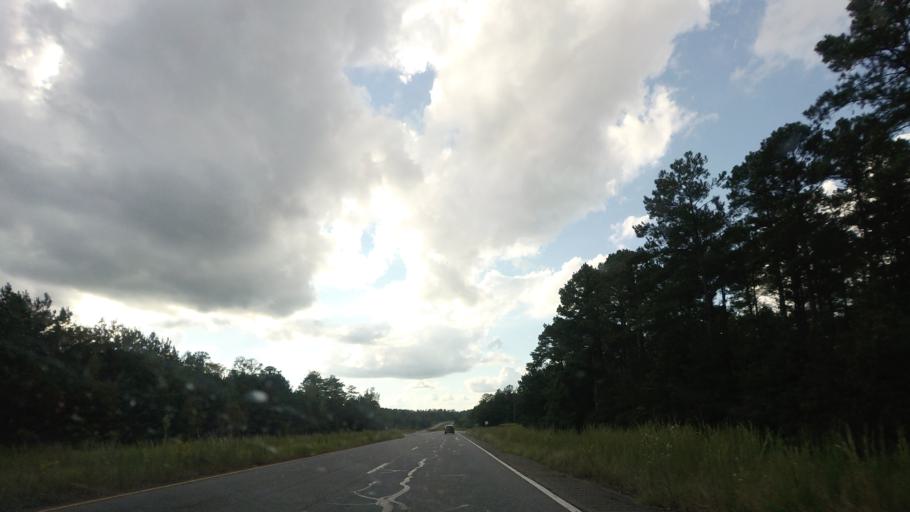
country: US
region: Georgia
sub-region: Houston County
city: Perry
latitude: 32.4158
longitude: -83.6896
